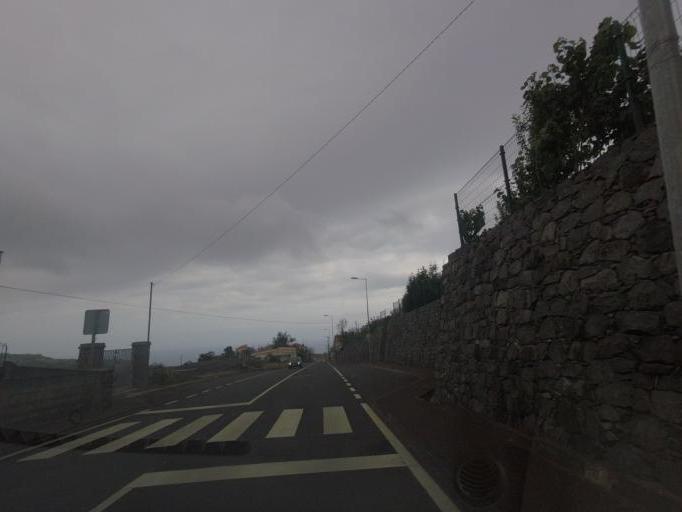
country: PT
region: Madeira
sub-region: Santana
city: Santana
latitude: 32.8183
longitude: -16.8874
